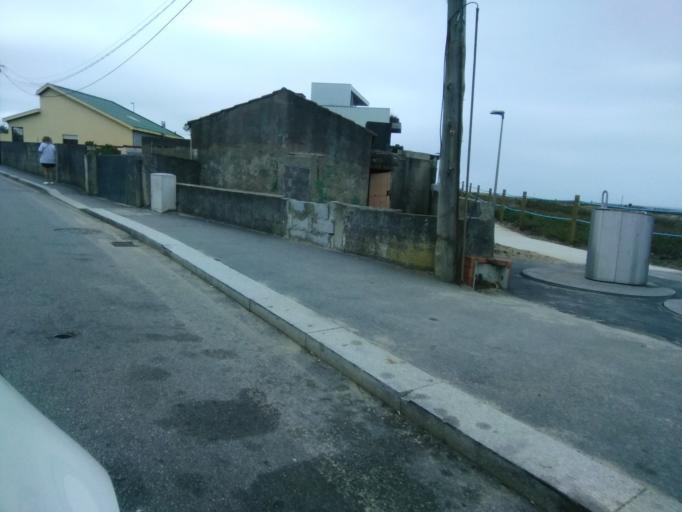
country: PT
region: Porto
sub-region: Matosinhos
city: Lavra
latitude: 41.2564
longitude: -8.7228
